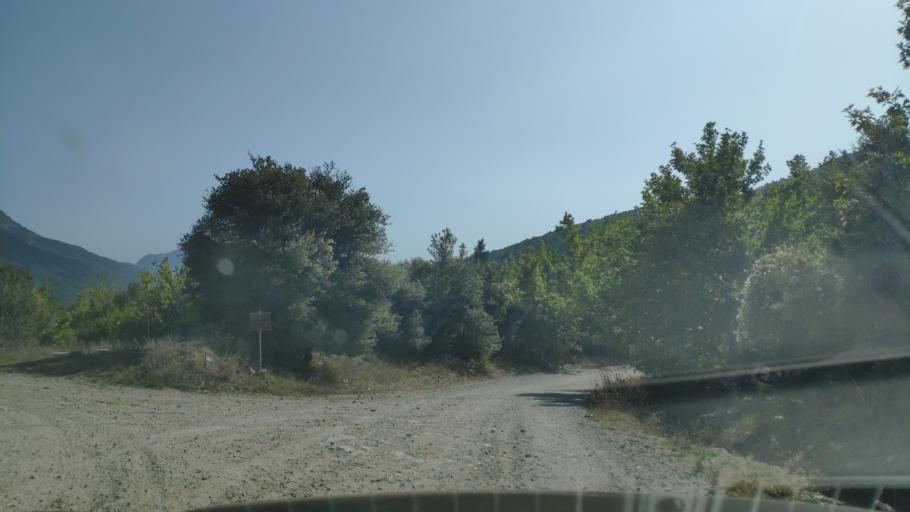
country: GR
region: West Greece
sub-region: Nomos Achaias
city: Aiyira
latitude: 37.9431
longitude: 22.3179
